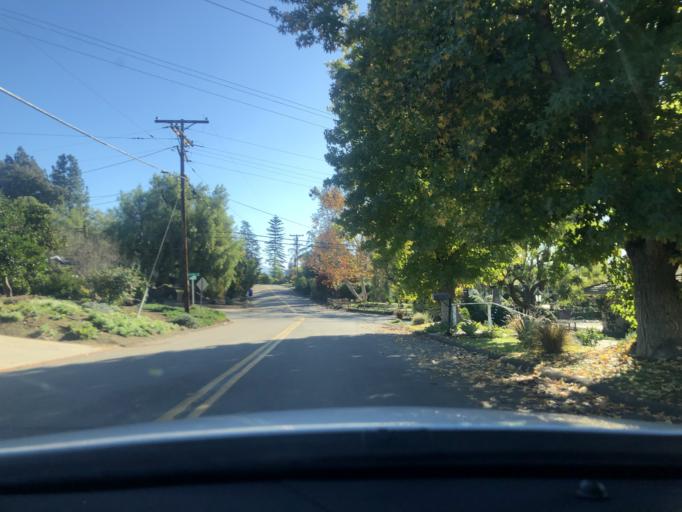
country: US
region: California
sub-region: San Diego County
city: Casa de Oro-Mount Helix
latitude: 32.7639
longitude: -116.9540
